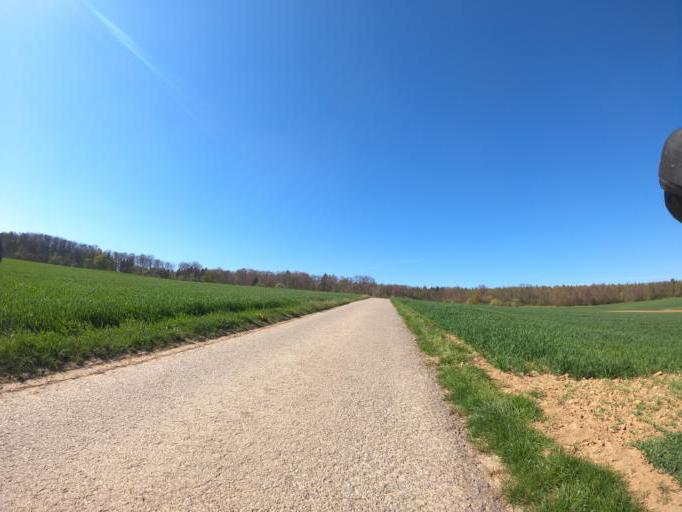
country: DE
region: Baden-Wuerttemberg
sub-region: Karlsruhe Region
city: Wiernsheim
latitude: 48.9148
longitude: 8.8752
